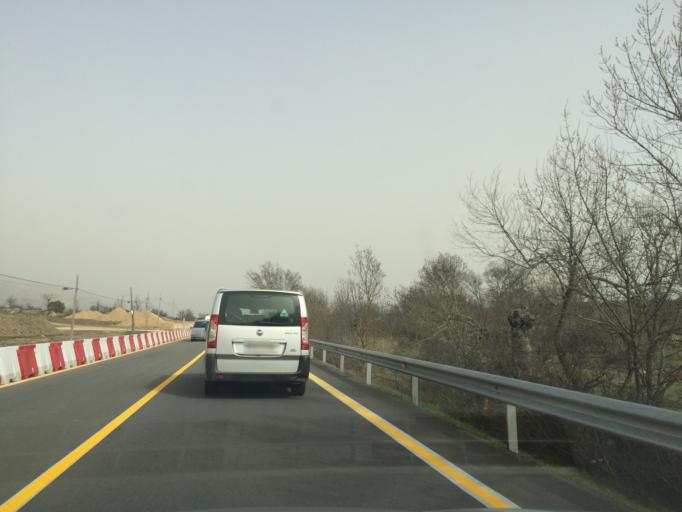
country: ES
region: Madrid
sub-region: Provincia de Madrid
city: Moralzarzal
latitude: 40.6885
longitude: -3.9512
